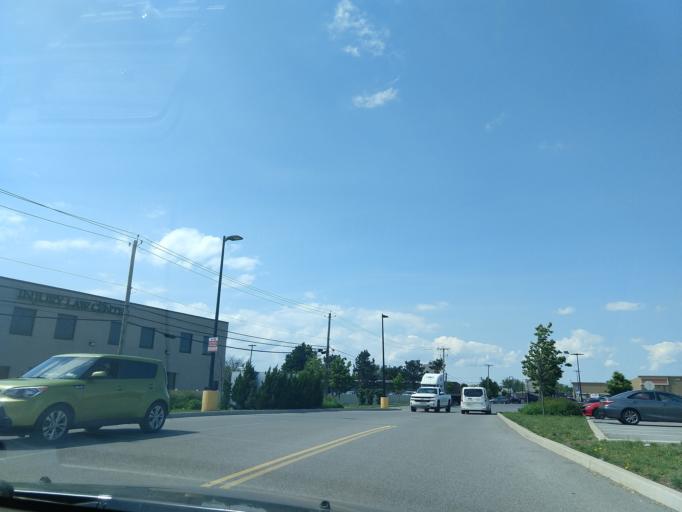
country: US
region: New York
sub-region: Erie County
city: Cheektowaga
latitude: 42.9084
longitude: -78.7447
